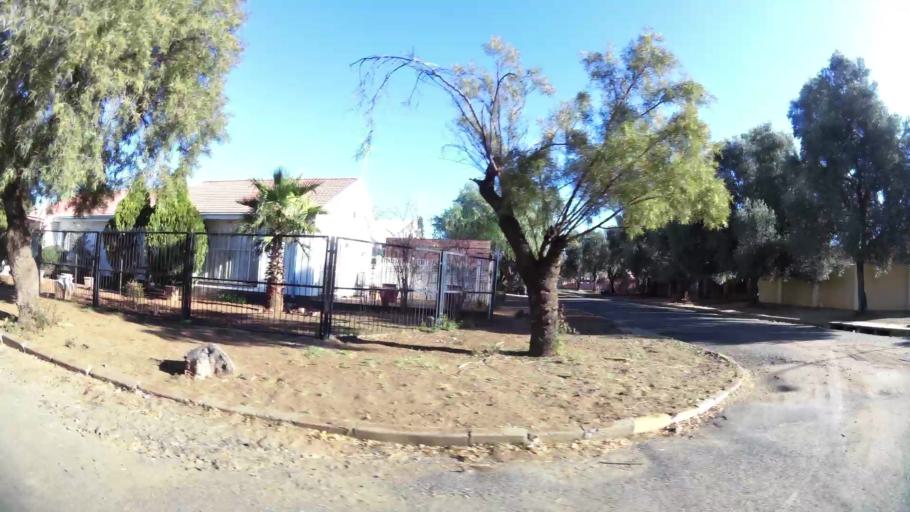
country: ZA
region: Northern Cape
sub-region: Frances Baard District Municipality
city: Kimberley
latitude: -28.7541
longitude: 24.7892
